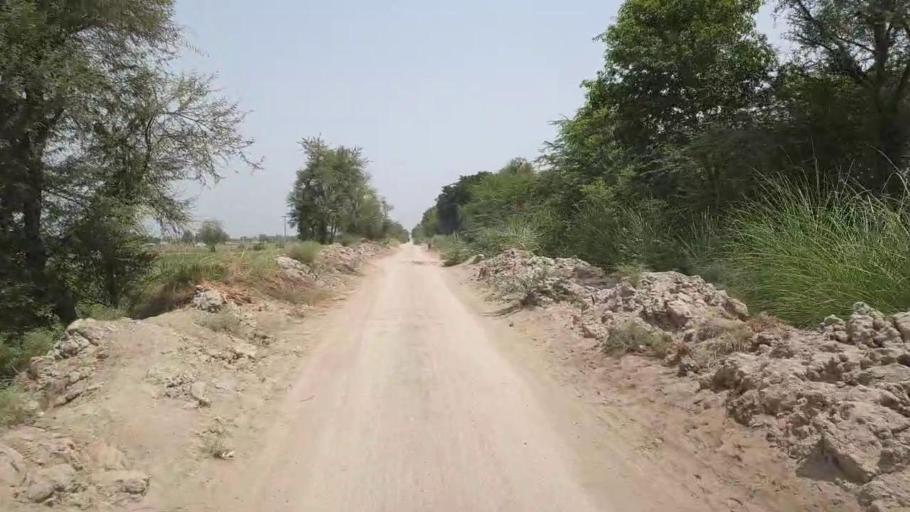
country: PK
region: Sindh
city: Nawabshah
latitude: 26.3097
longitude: 68.3018
